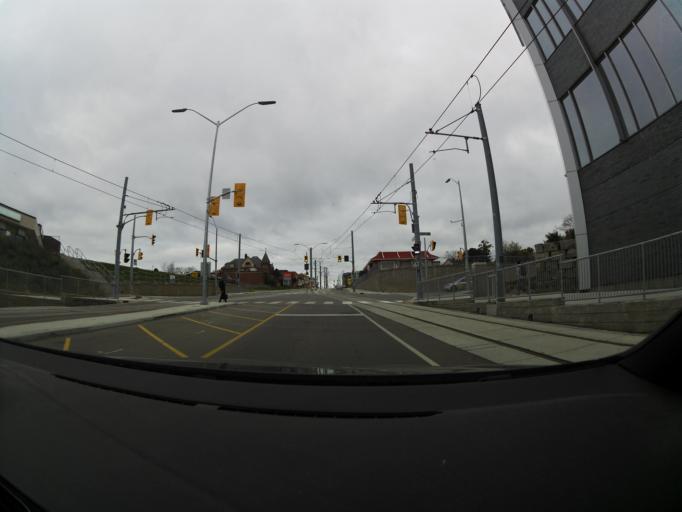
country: CA
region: Ontario
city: Waterloo
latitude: 43.4536
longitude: -80.5006
